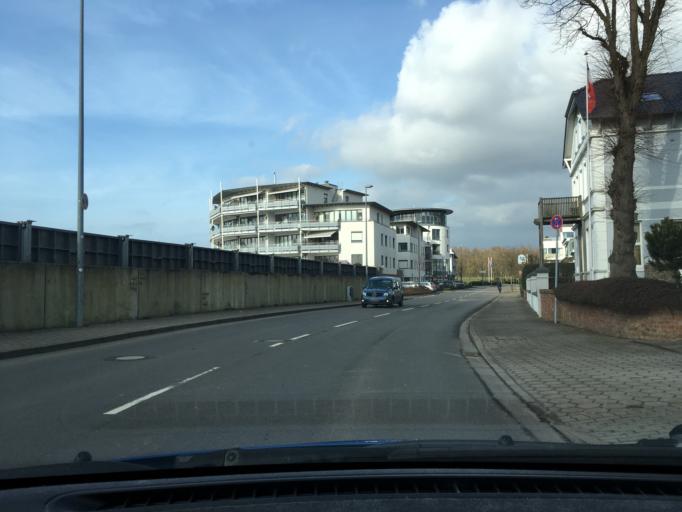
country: DE
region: Schleswig-Holstein
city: Wedel
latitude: 53.5708
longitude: 9.6993
